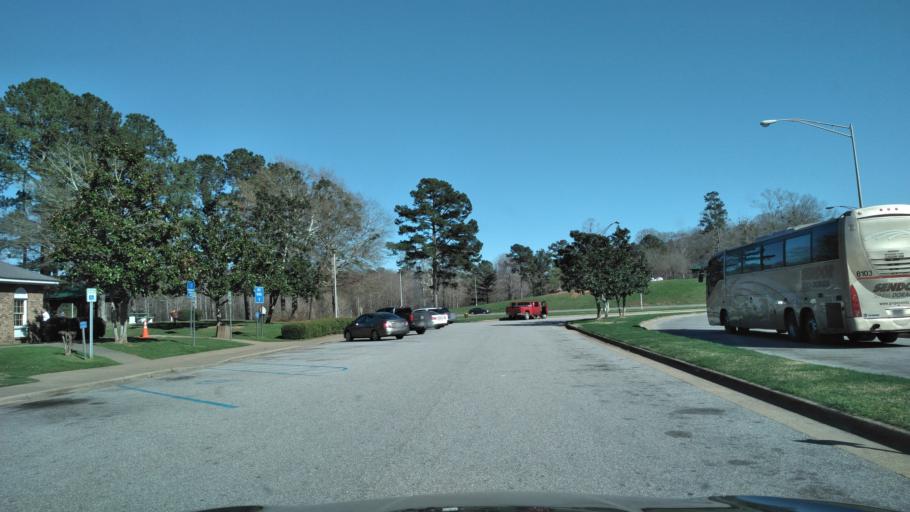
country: US
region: Alabama
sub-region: Butler County
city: Greenville
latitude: 31.8845
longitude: -86.6106
